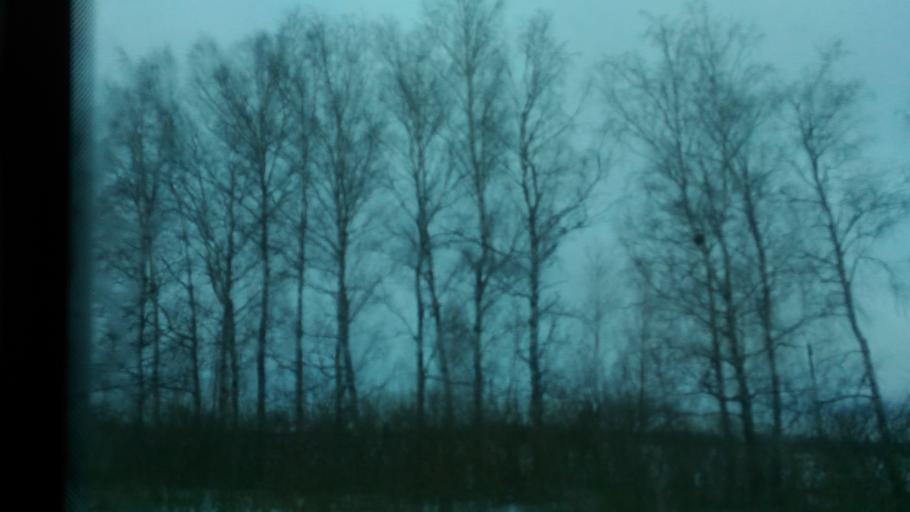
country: RU
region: Tula
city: Bolokhovo
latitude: 54.0581
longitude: 37.8057
